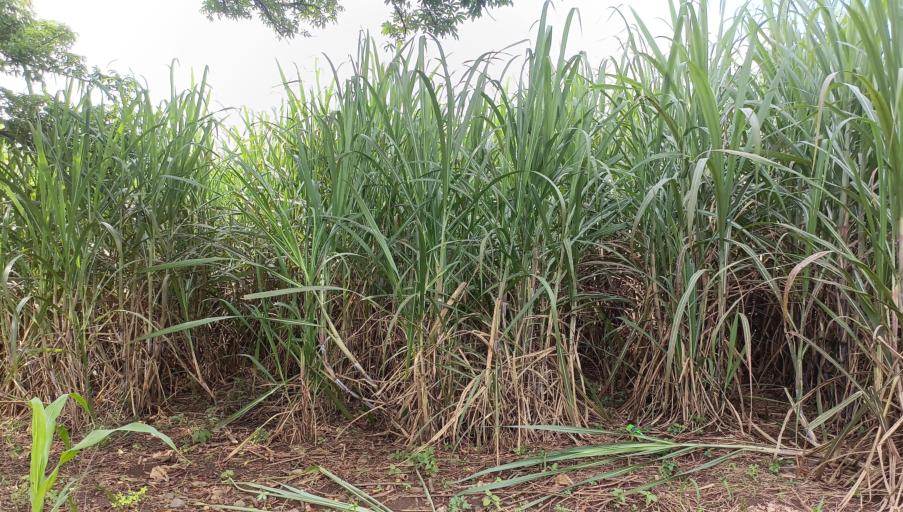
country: PH
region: Northern Mindanao
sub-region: Province of Bukidnon
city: Dologon
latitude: 7.8328
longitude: 125.0439
